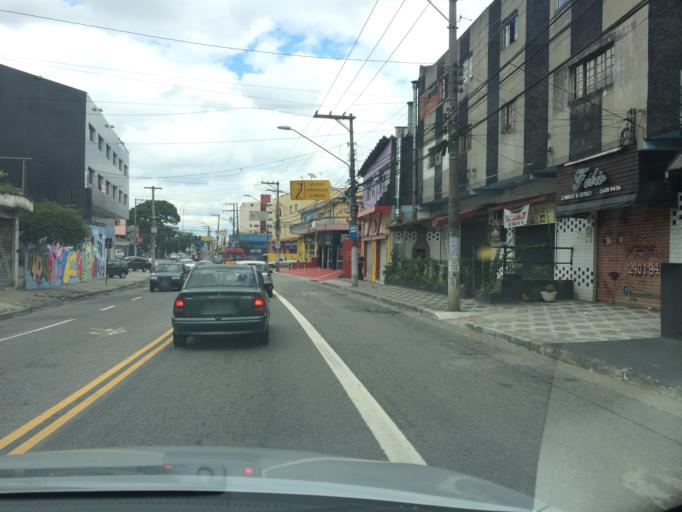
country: BR
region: Sao Paulo
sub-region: Guarulhos
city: Guarulhos
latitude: -23.4471
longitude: -46.5212
